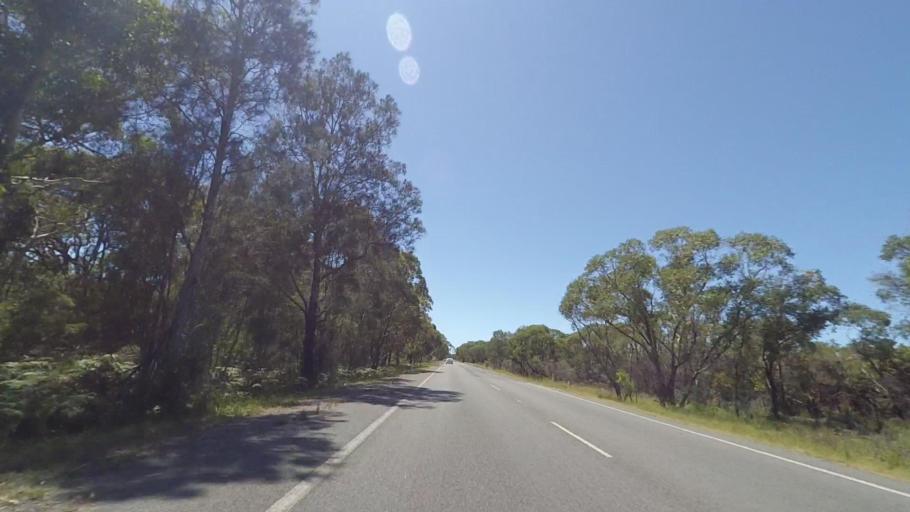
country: AU
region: New South Wales
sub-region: Port Stephens Shire
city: Medowie
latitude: -32.7796
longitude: 151.8825
